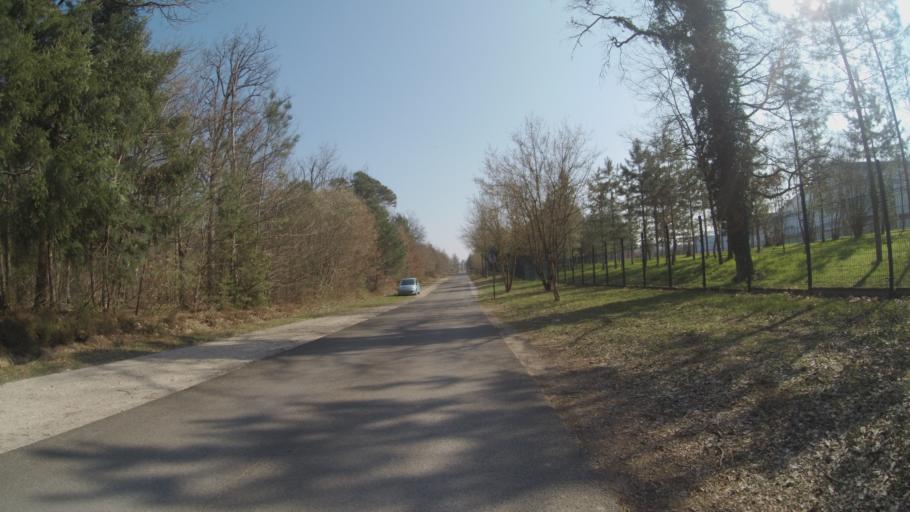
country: FR
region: Centre
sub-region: Departement du Loiret
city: Boigny-sur-Bionne
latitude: 47.9320
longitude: 1.9973
